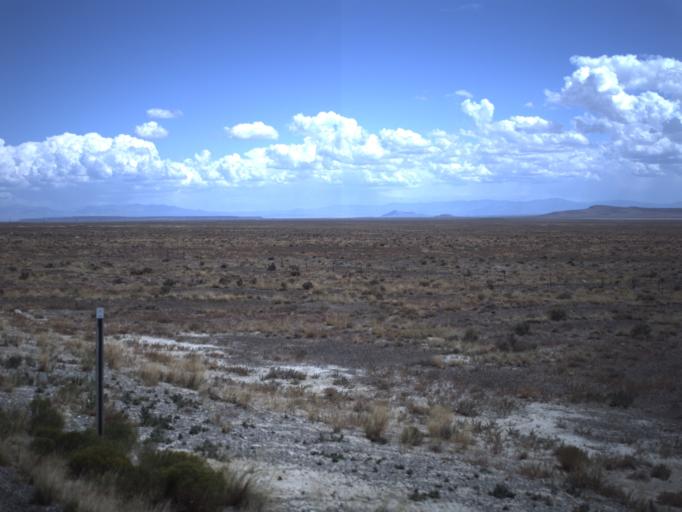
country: US
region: Utah
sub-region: Millard County
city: Delta
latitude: 39.1545
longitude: -113.0619
